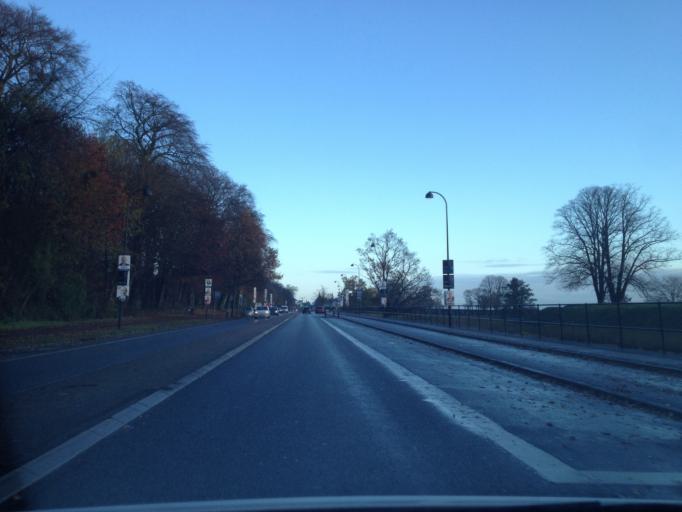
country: DK
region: Capital Region
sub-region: Gentofte Kommune
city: Charlottenlund
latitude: 55.7462
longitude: 12.5851
